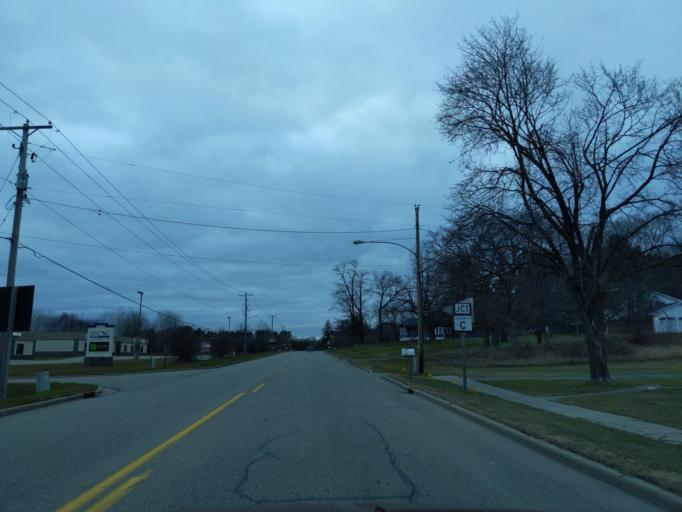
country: US
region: Wisconsin
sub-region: Waushara County
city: Wautoma
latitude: 44.0770
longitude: -89.2977
